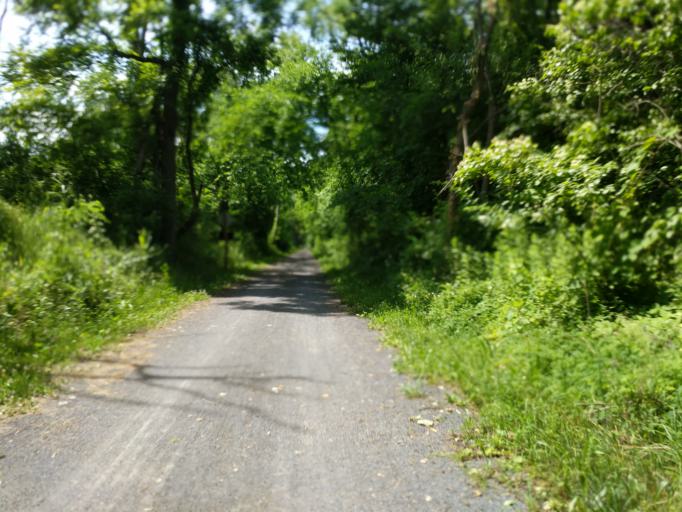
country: US
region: New York
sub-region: Tompkins County
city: Northwest Ithaca
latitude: 42.5134
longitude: -76.5621
